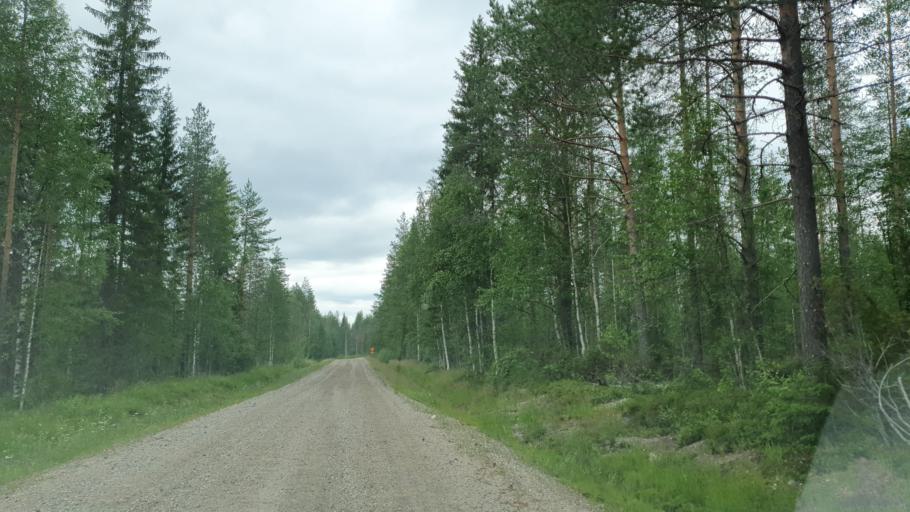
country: FI
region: Kainuu
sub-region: Kehys-Kainuu
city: Kuhmo
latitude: 64.0110
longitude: 29.3444
